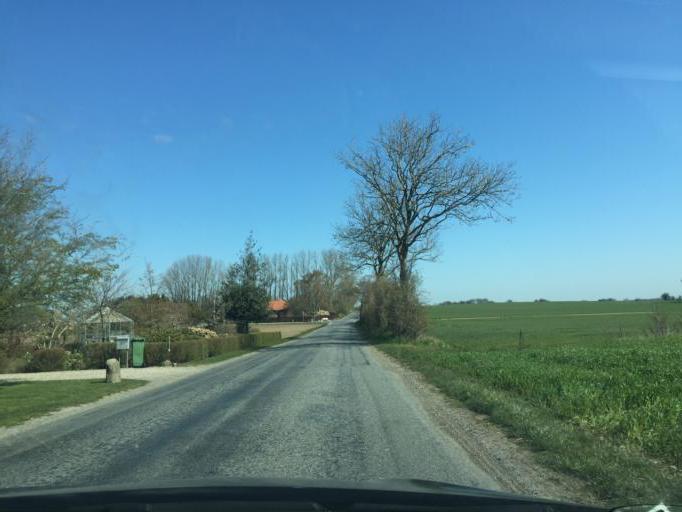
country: DK
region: South Denmark
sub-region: Faaborg-Midtfyn Kommune
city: Ringe
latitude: 55.2685
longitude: 10.5279
